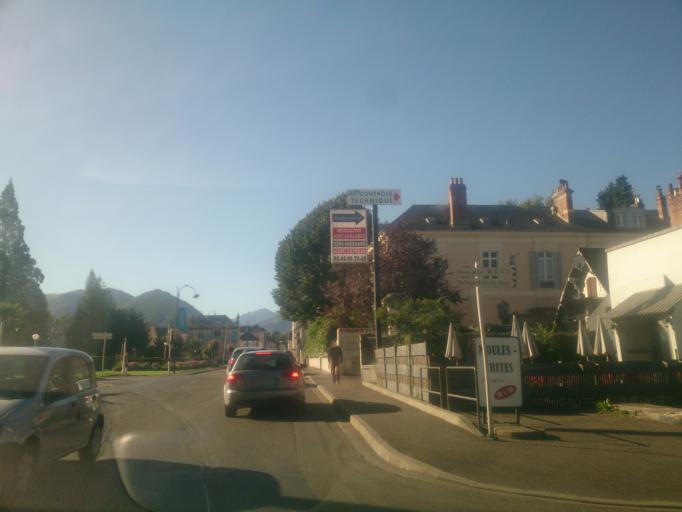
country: FR
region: Midi-Pyrenees
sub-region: Departement des Hautes-Pyrenees
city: Bagneres-de-Bigorre
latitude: 43.0694
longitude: 0.1462
